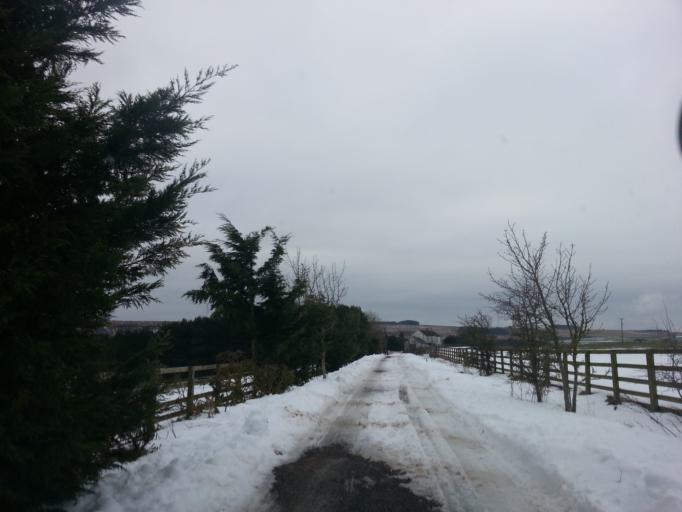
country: GB
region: England
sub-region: County Durham
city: Tow Law
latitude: 54.7709
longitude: -1.7931
